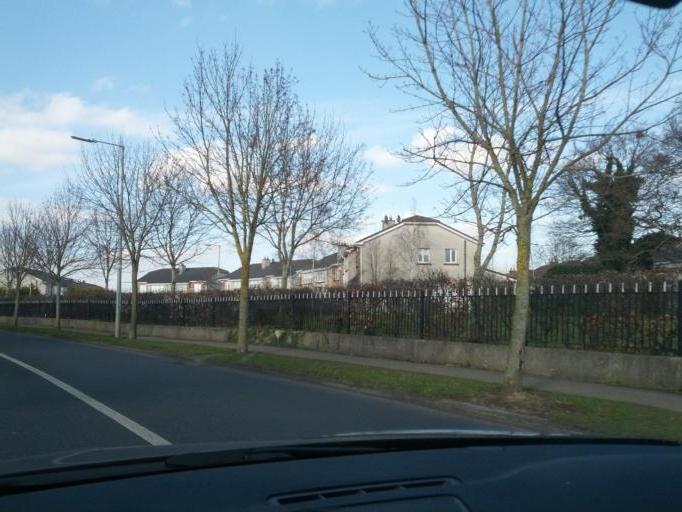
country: IE
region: Leinster
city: Clondalkin
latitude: 53.3444
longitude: -6.4187
